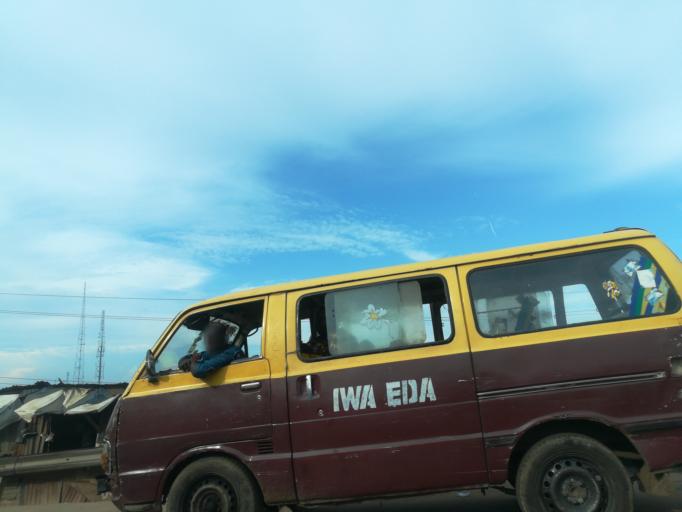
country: NG
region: Oyo
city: Ibadan
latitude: 7.3833
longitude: 3.9312
